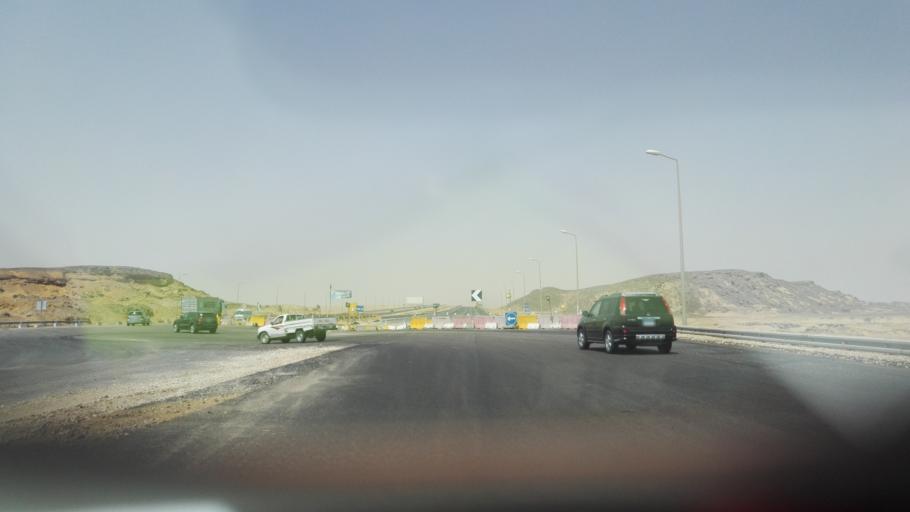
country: EG
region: As Suways
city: Ain Sukhna
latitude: 29.7097
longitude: 32.0814
